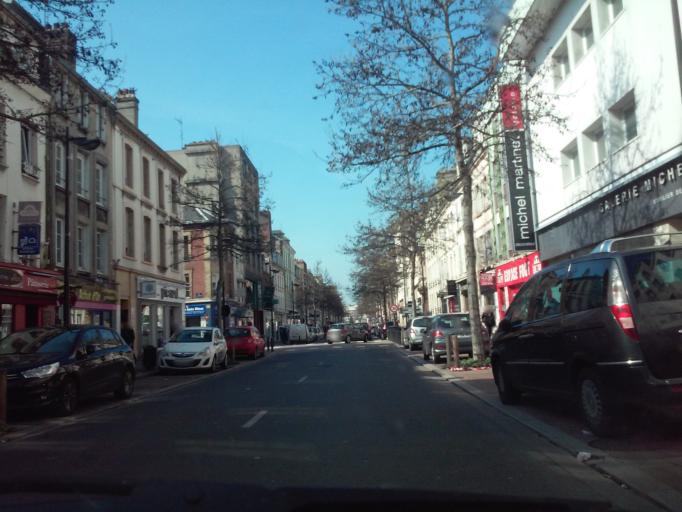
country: FR
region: Haute-Normandie
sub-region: Departement de la Seine-Maritime
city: Le Havre
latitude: 49.4982
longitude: 0.1159
